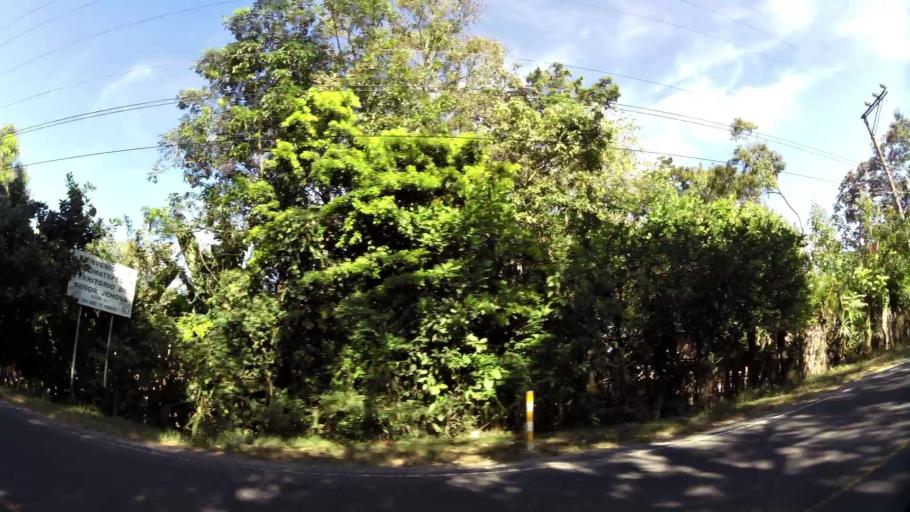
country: SV
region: Cuscatlan
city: Tecoluca
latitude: 13.8282
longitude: -89.0284
